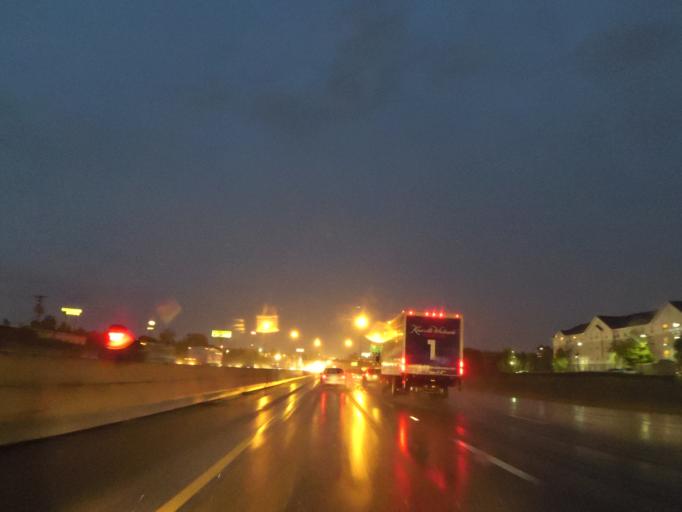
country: US
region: Tennessee
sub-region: Knox County
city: Farragut
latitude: 35.9047
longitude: -84.1509
